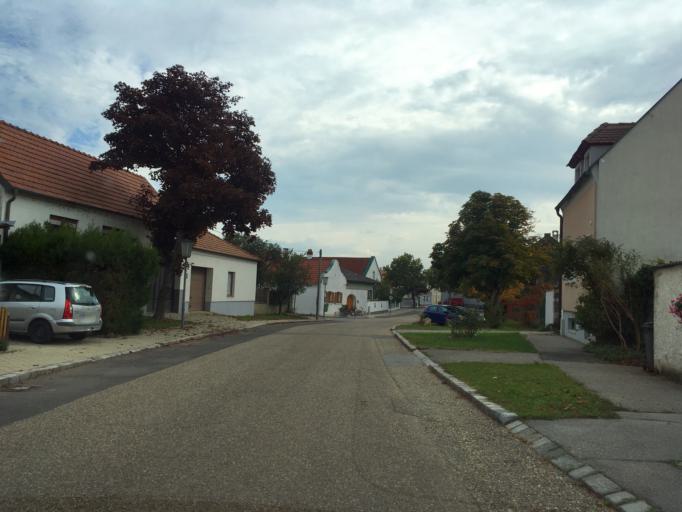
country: AT
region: Burgenland
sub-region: Politischer Bezirk Neusiedl am See
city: Winden am See
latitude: 47.9530
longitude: 16.7511
